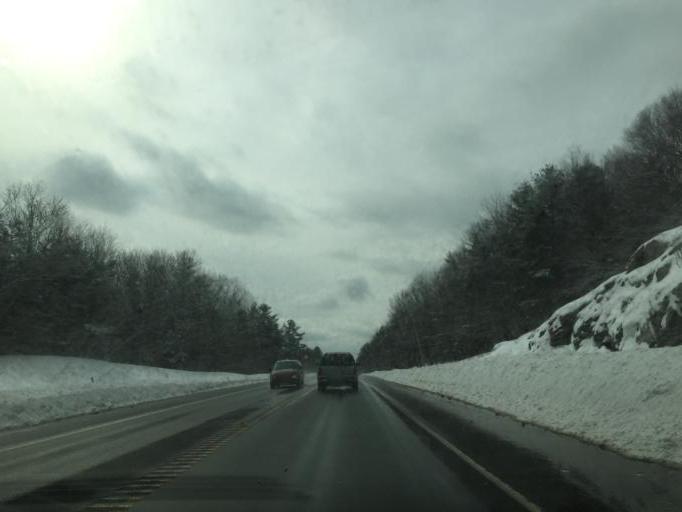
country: US
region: New Hampshire
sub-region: Carroll County
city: Sanbornville
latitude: 43.5161
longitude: -71.0285
